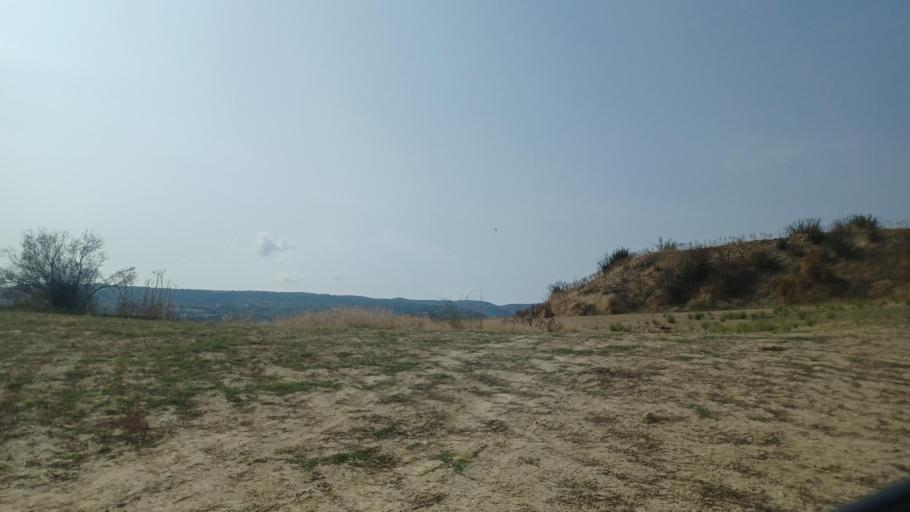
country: CY
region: Pafos
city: Polis
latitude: 34.9739
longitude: 32.4583
